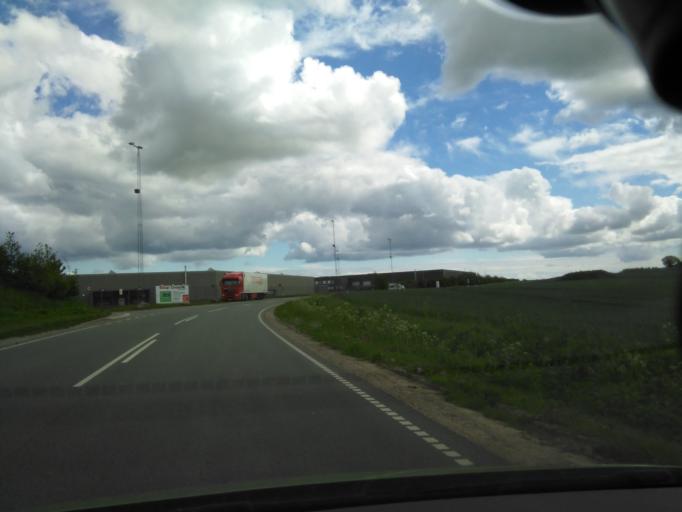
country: DK
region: Central Jutland
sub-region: Arhus Kommune
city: Kolt
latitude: 56.0992
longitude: 10.0654
